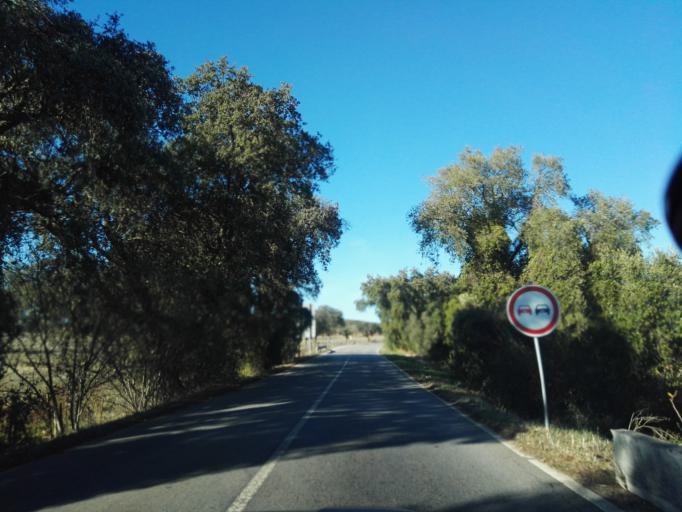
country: PT
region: Portalegre
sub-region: Elvas
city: Elvas
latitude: 38.9119
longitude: -7.1812
